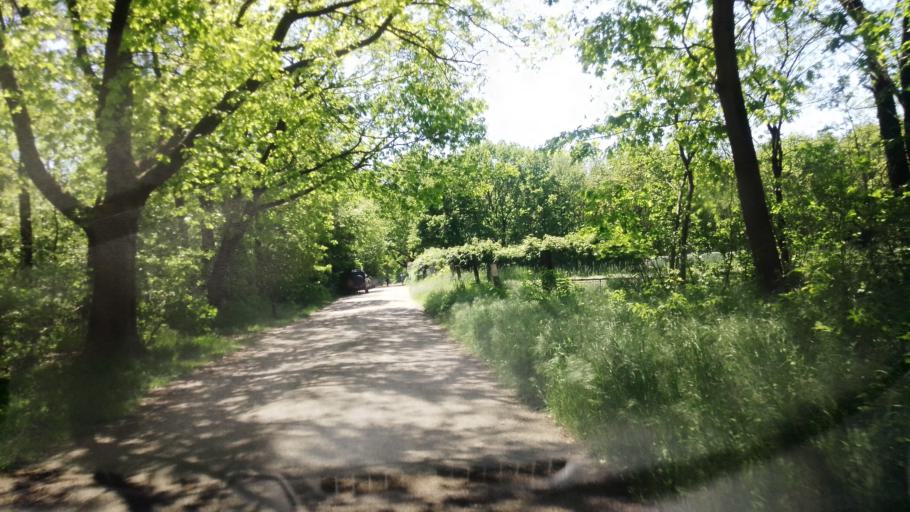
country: NL
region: Limburg
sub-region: Gemeente Venlo
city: Tegelen
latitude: 51.3275
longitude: 6.1553
